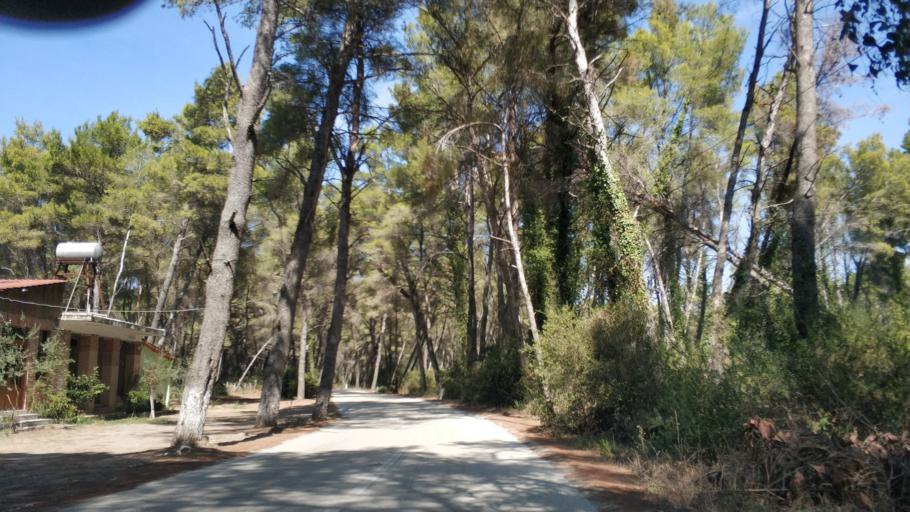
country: AL
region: Fier
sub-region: Rrethi i Lushnjes
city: Divjake
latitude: 40.9751
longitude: 19.4809
